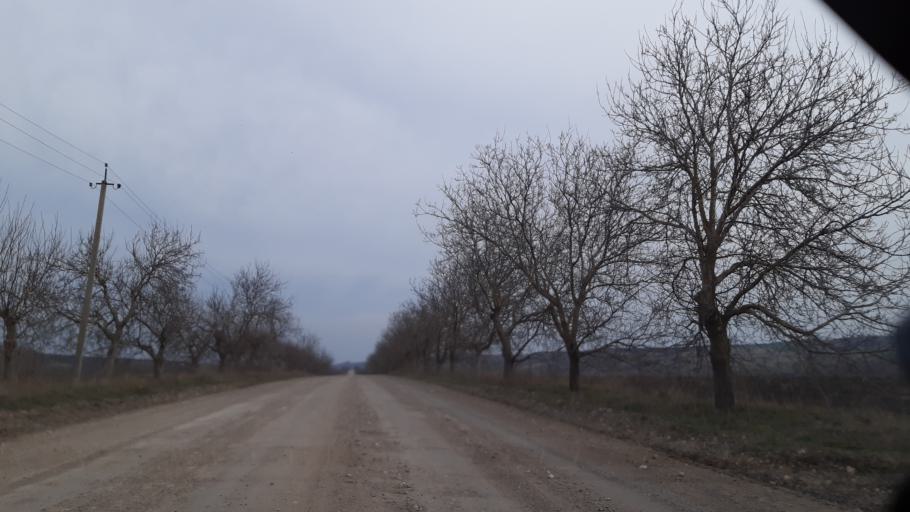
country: MD
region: Soldanesti
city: Soldanesti
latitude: 47.7008
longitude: 28.7225
